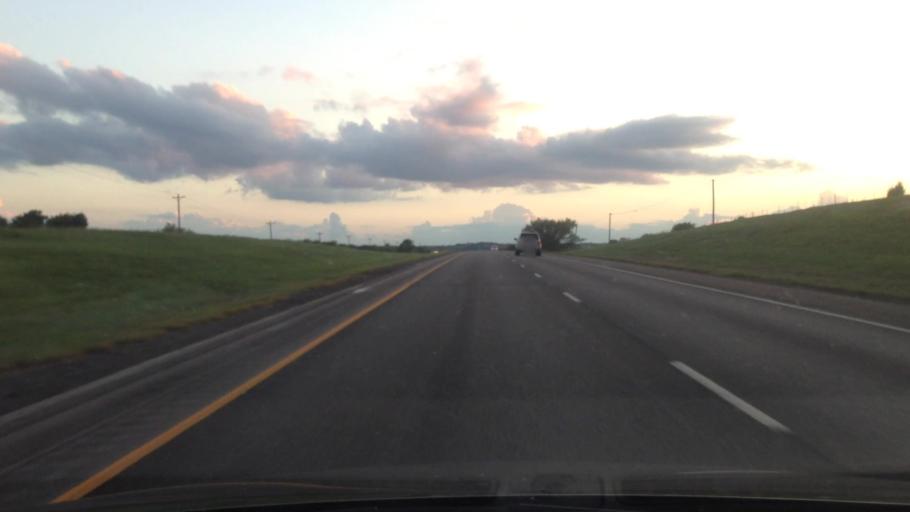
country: US
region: Texas
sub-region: Parker County
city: Aledo
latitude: 32.5944
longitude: -97.5818
